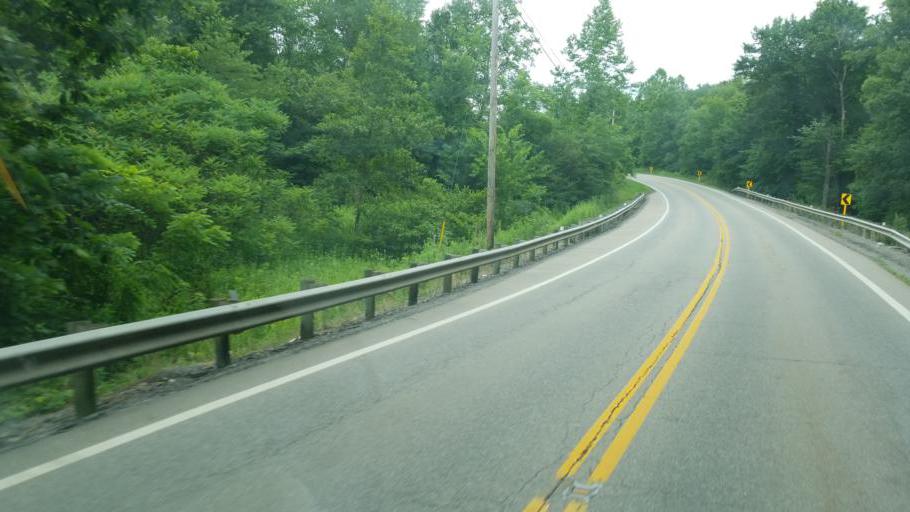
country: US
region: Ohio
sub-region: Columbiana County
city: Salineville
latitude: 40.6945
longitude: -80.8058
